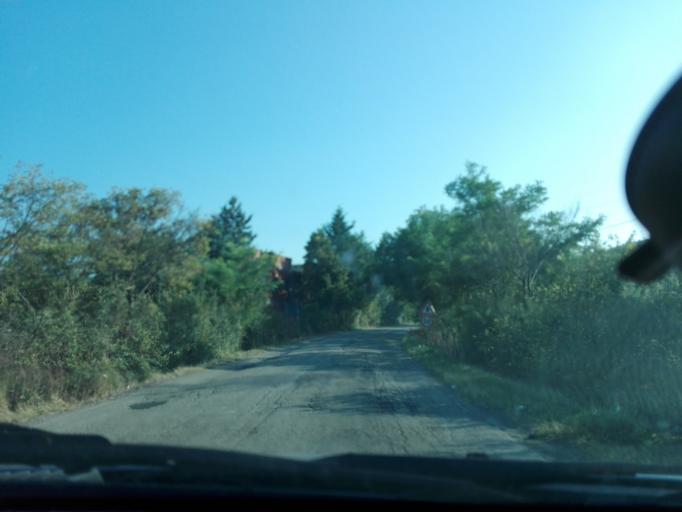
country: IT
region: Abruzzo
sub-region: Provincia di Pescara
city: Cappelle sul Tavo
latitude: 42.4521
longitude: 14.0900
